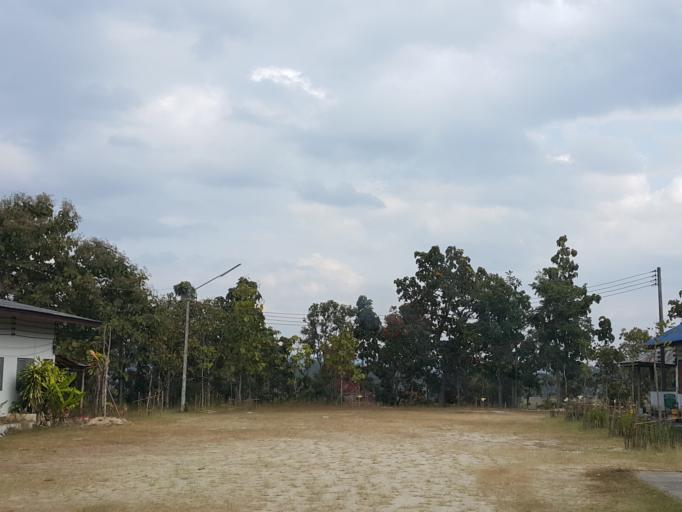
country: TH
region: Chiang Mai
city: Om Koi
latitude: 17.7974
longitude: 98.3395
